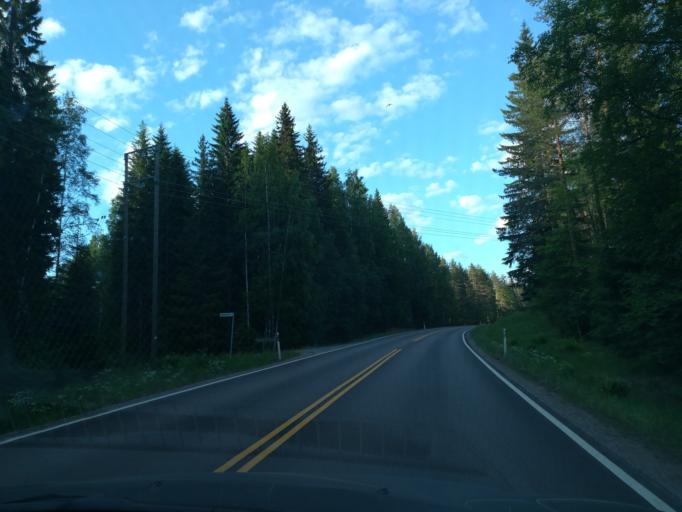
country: FI
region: Southern Savonia
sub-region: Mikkeli
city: Puumala
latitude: 61.5772
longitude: 28.1593
